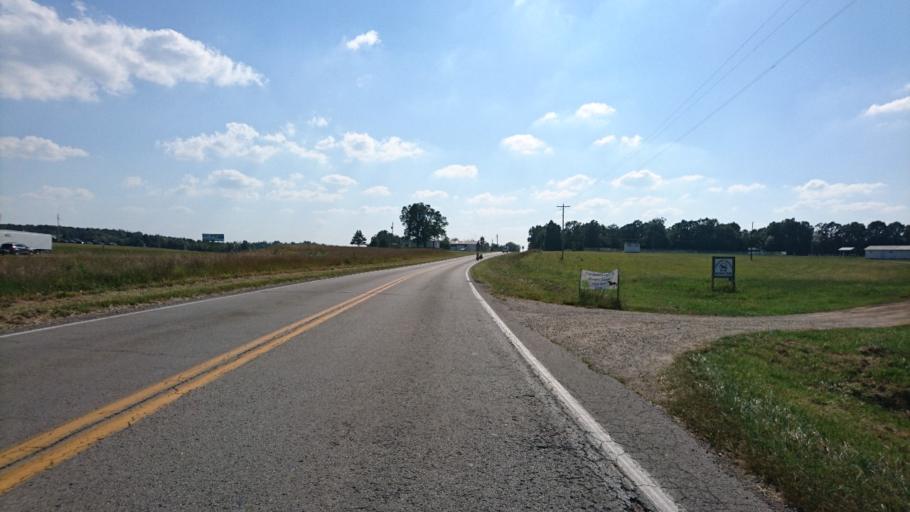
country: US
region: Missouri
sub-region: Laclede County
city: Lebanon
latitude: 37.6406
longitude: -92.6752
